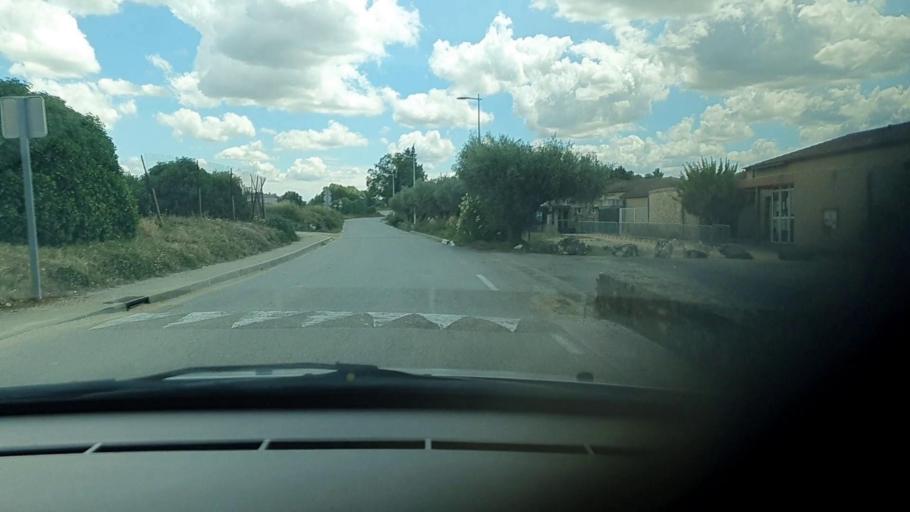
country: FR
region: Languedoc-Roussillon
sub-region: Departement du Gard
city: Moussac
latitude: 44.0503
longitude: 4.2285
